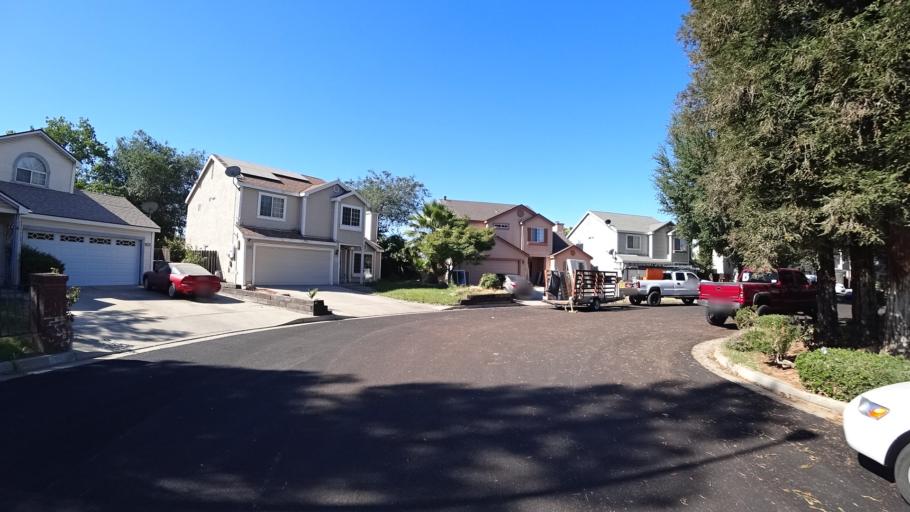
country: US
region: California
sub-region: Fresno County
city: West Park
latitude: 36.7844
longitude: -119.8558
